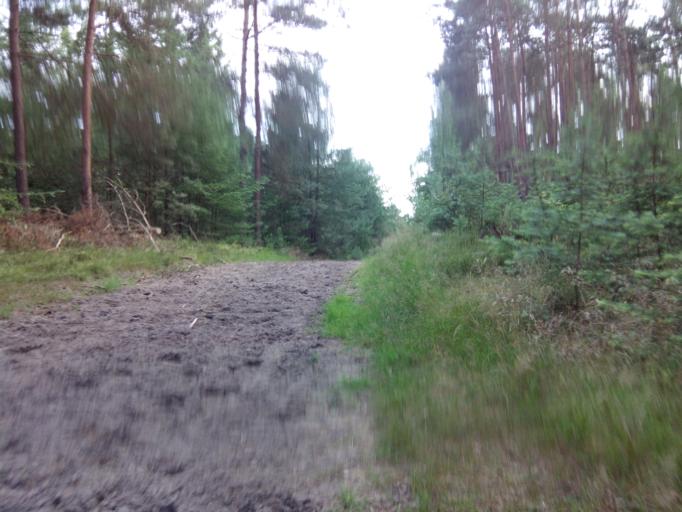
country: NL
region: Utrecht
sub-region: Gemeente Utrechtse Heuvelrug
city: Maarn
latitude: 52.0873
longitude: 5.3626
